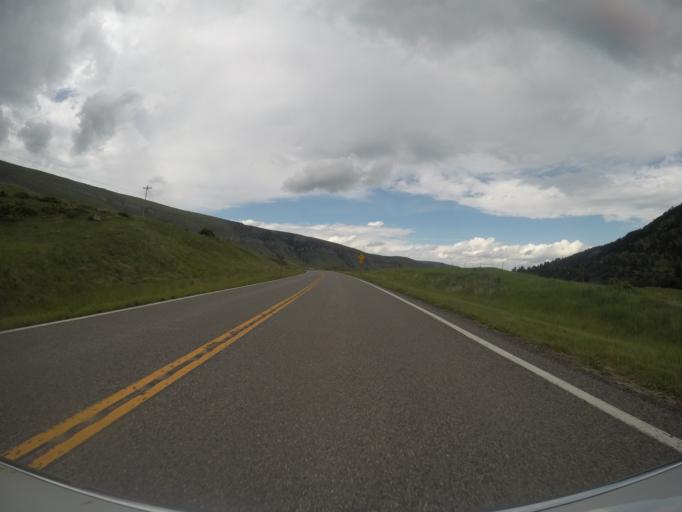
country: US
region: Montana
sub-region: Sweet Grass County
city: Big Timber
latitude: 45.5613
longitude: -110.2019
